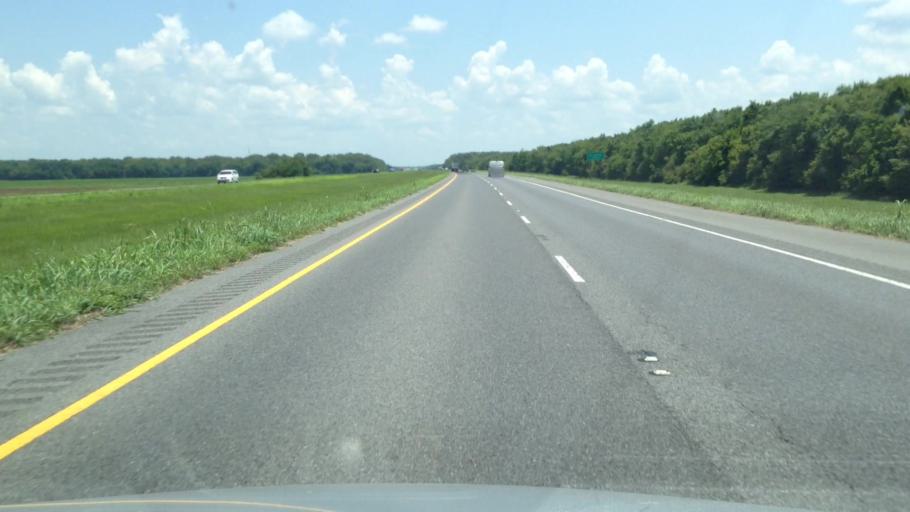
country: US
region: Louisiana
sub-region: Evangeline Parish
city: Ville Platte
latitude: 30.8033
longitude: -92.2123
